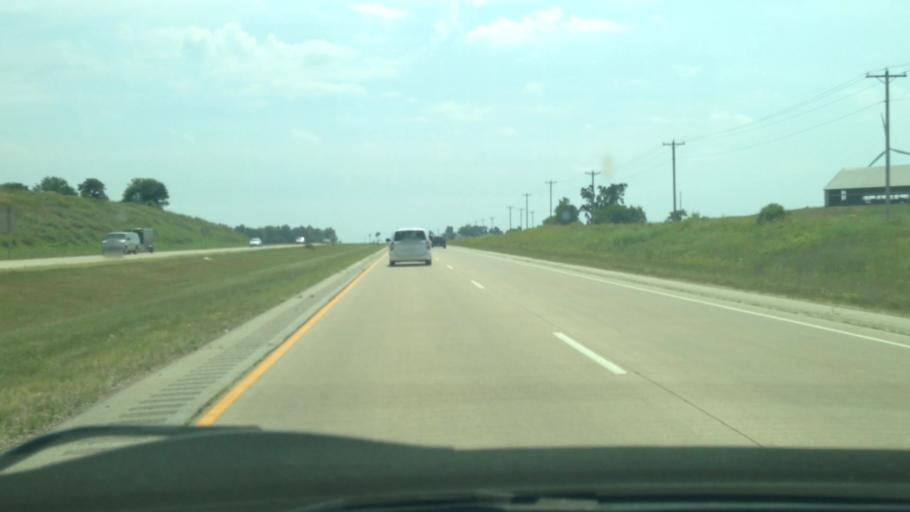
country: US
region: Wisconsin
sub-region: Dane County
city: Waunakee
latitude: 43.1855
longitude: -89.5535
